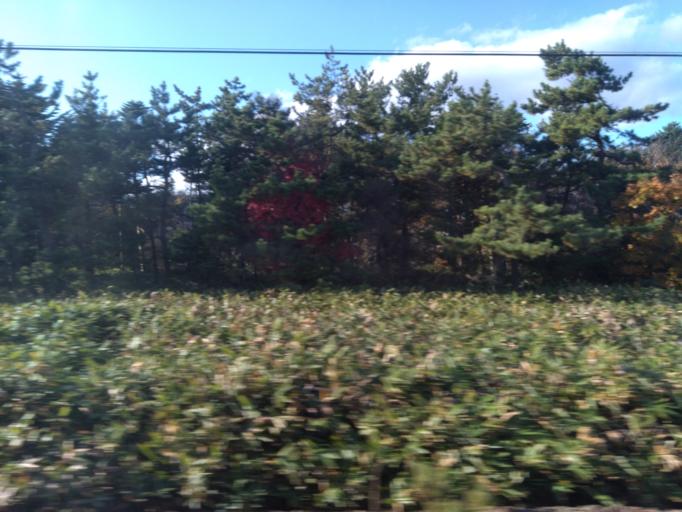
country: JP
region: Hokkaido
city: Niseko Town
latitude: 42.5737
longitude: 140.4462
